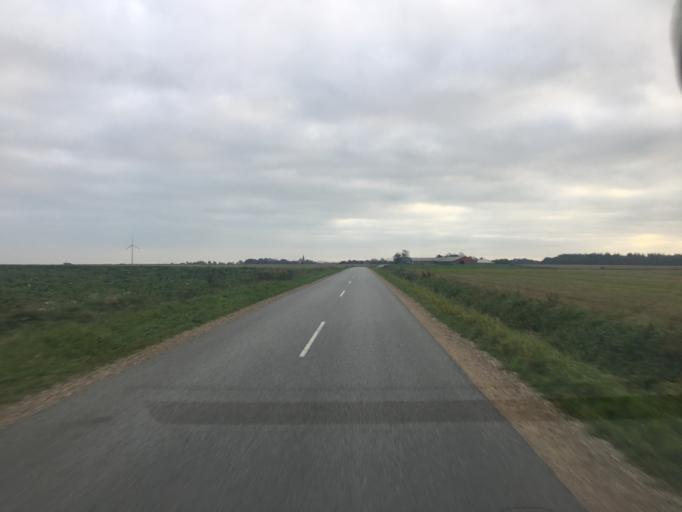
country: DE
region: Schleswig-Holstein
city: Aventoft
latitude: 54.9850
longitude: 8.7552
